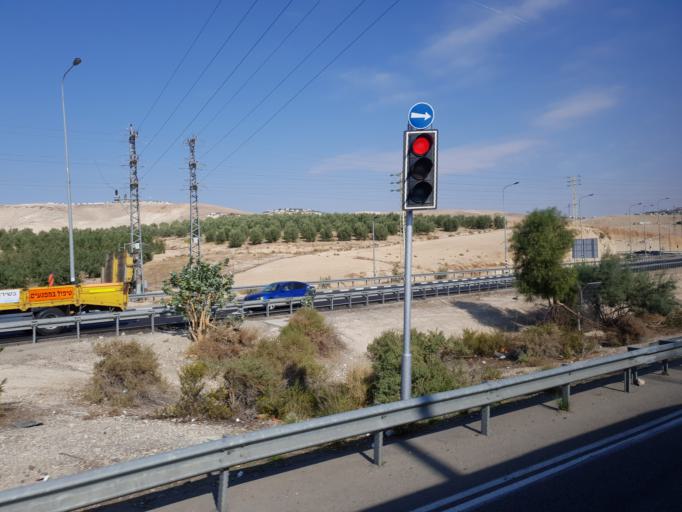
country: PS
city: Az Za`ayyim
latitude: 31.8044
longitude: 35.3251
